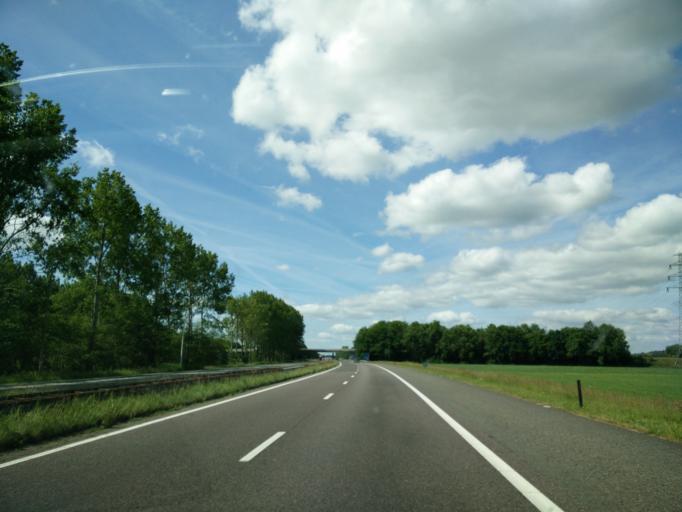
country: NL
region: Drenthe
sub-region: Gemeente Assen
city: Assen
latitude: 53.0213
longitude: 6.5520
